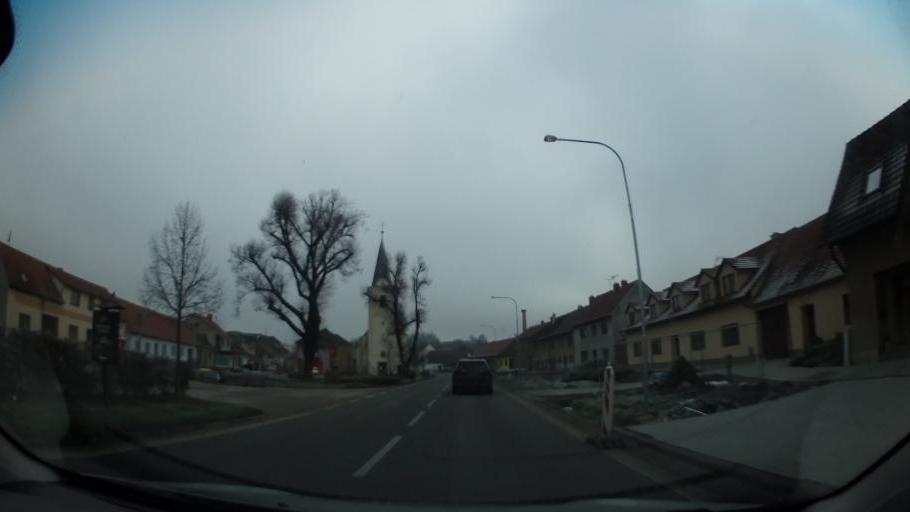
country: CZ
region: Vysocina
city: Vladislav
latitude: 49.2103
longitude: 15.9868
